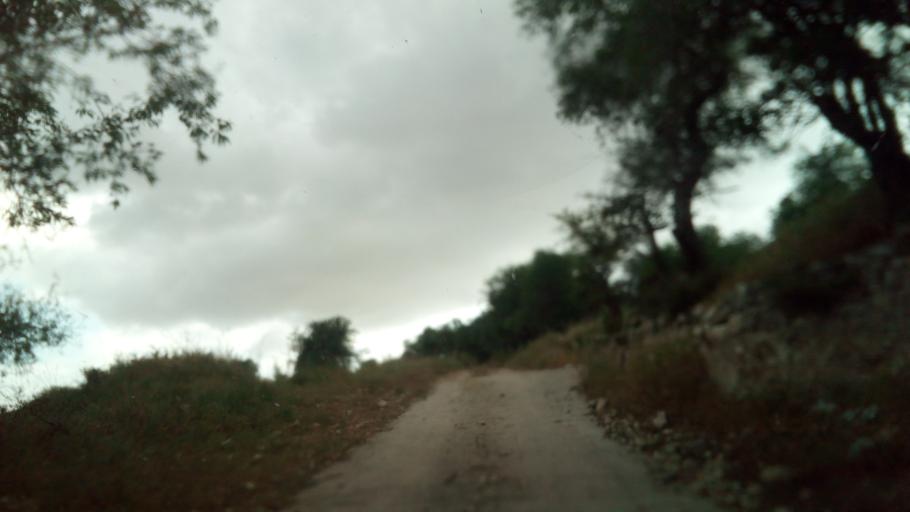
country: CY
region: Pafos
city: Mesogi
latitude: 34.7675
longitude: 32.5645
